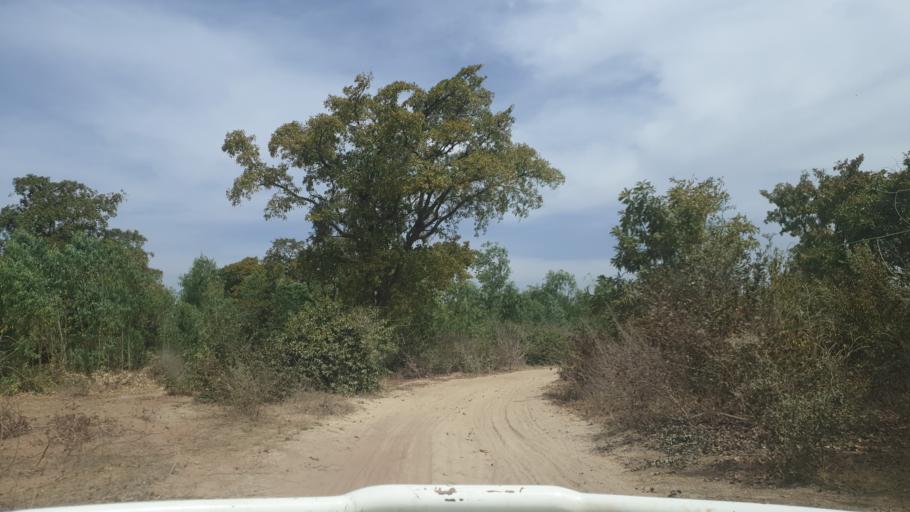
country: ML
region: Sikasso
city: Yorosso
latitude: 12.2419
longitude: -4.7330
